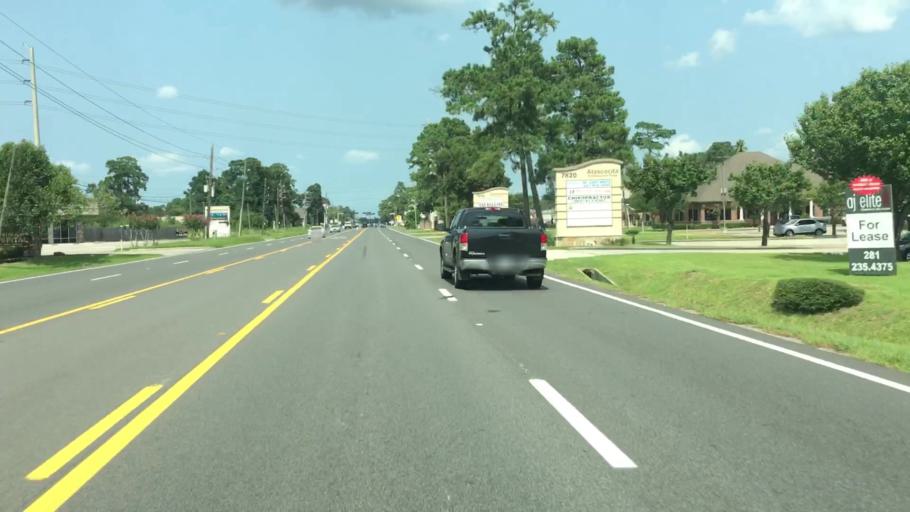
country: US
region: Texas
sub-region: Harris County
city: Atascocita
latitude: 30.0023
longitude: -95.1577
